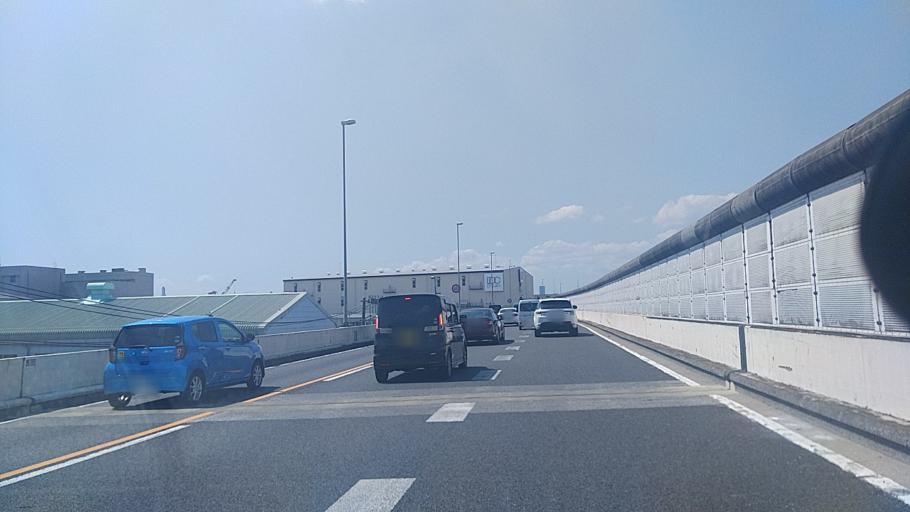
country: JP
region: Kanagawa
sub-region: Kawasaki-shi
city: Kawasaki
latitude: 35.5024
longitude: 139.6998
